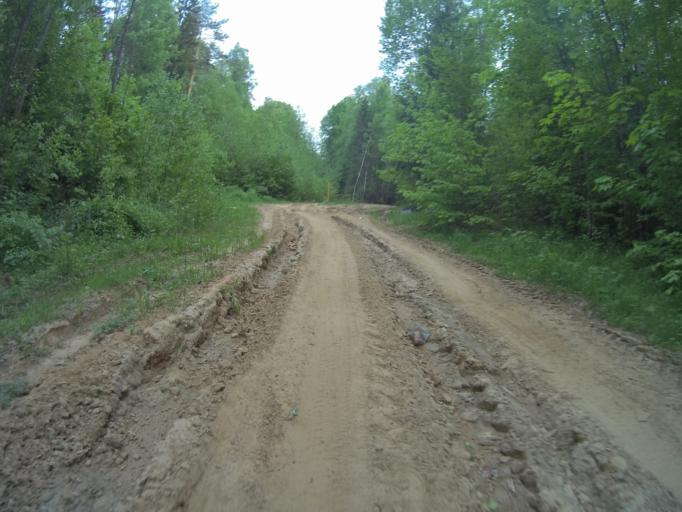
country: RU
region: Vladimir
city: Golovino
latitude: 56.0165
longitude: 40.4500
